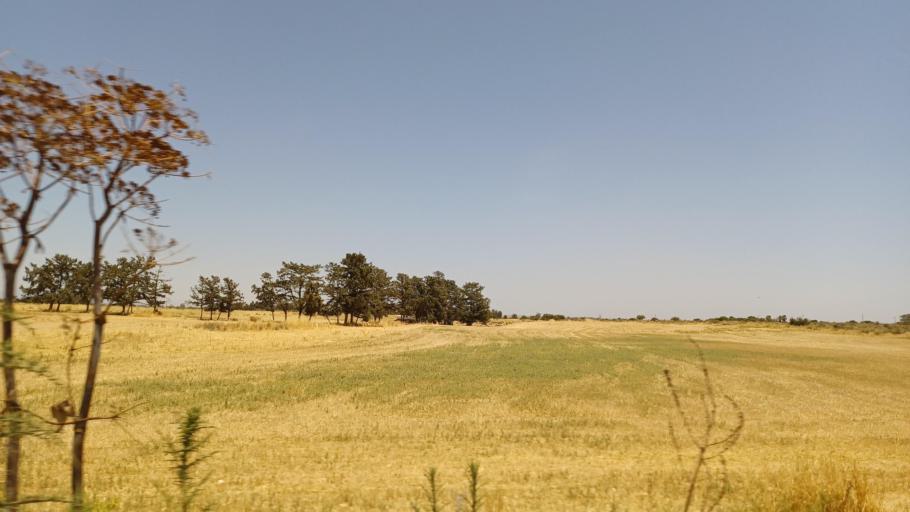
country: CY
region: Larnaka
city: Pergamos
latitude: 35.0259
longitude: 33.7067
